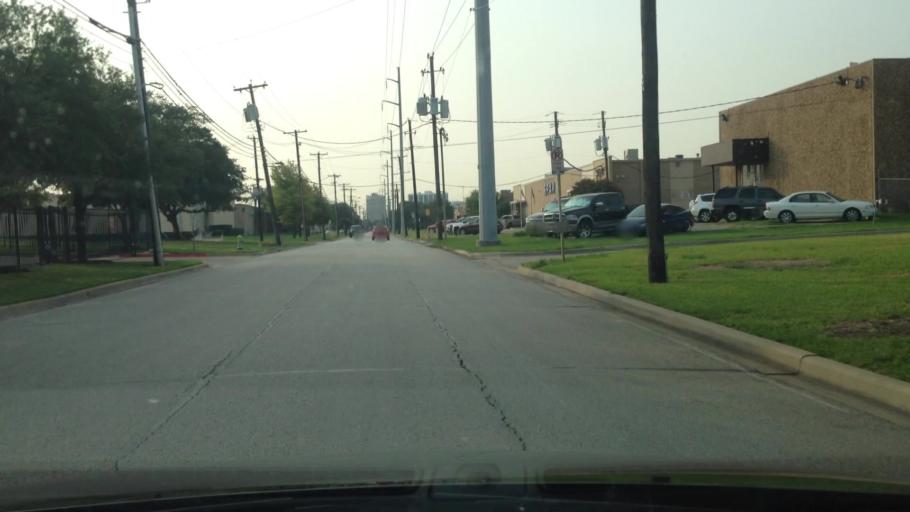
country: US
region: Texas
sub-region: Dallas County
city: Irving
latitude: 32.8286
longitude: -96.8835
